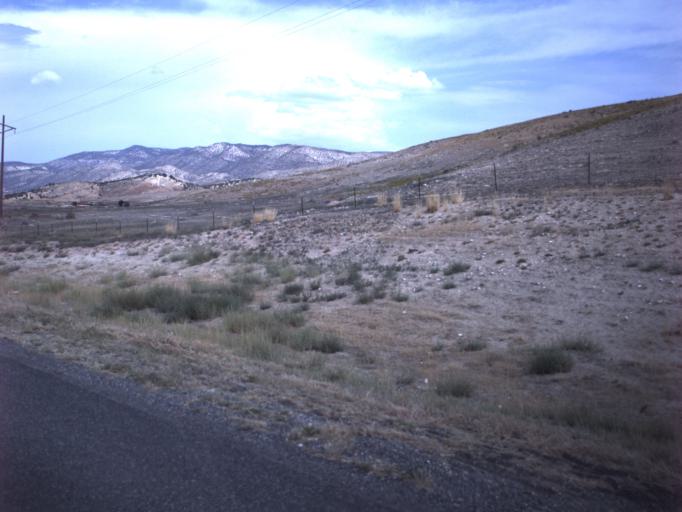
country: US
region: Utah
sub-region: Sanpete County
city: Gunnison
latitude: 39.2033
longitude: -111.8471
